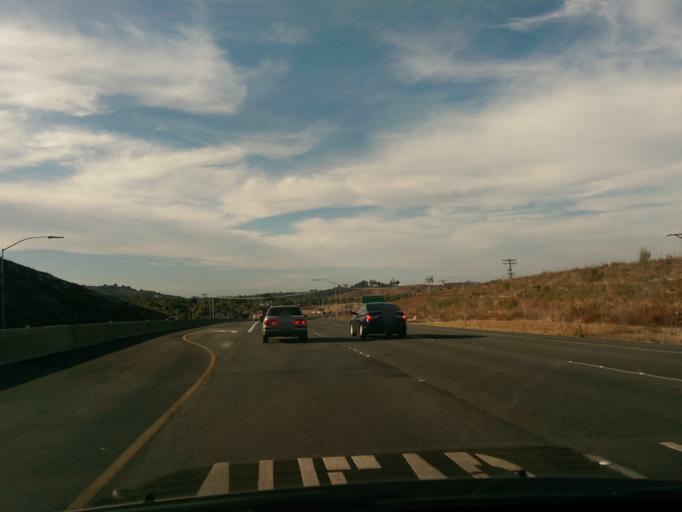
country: US
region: California
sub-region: San Diego County
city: Bonsall
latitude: 33.2859
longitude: -117.2254
